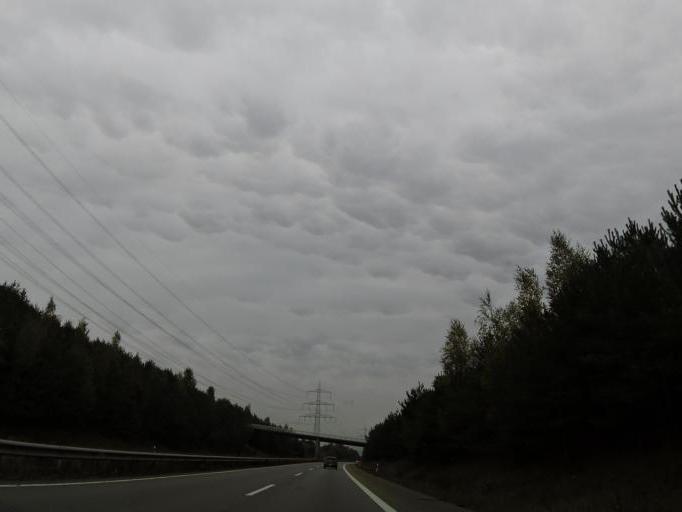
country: DE
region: Rheinland-Pfalz
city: Wartenberg-Rohrbach
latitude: 49.5256
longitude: 7.8456
